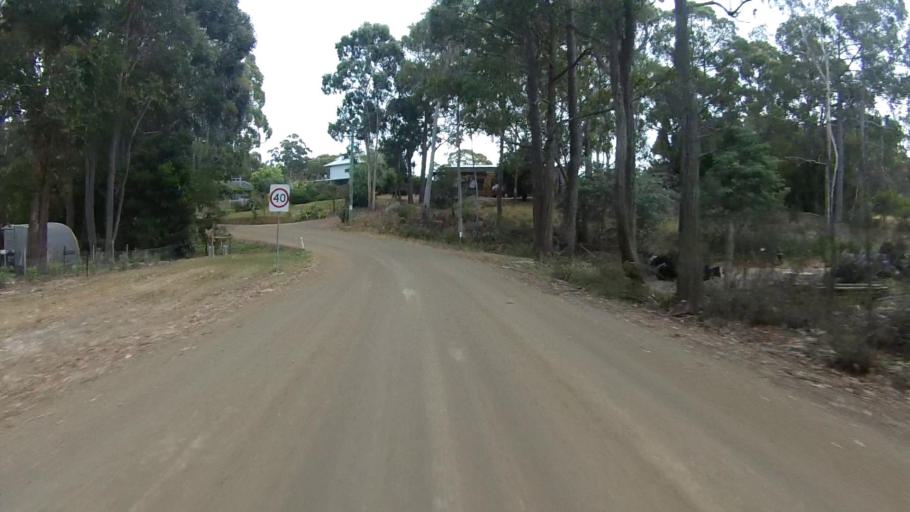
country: AU
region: Tasmania
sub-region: Huon Valley
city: Cygnet
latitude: -43.2284
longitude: 147.0978
